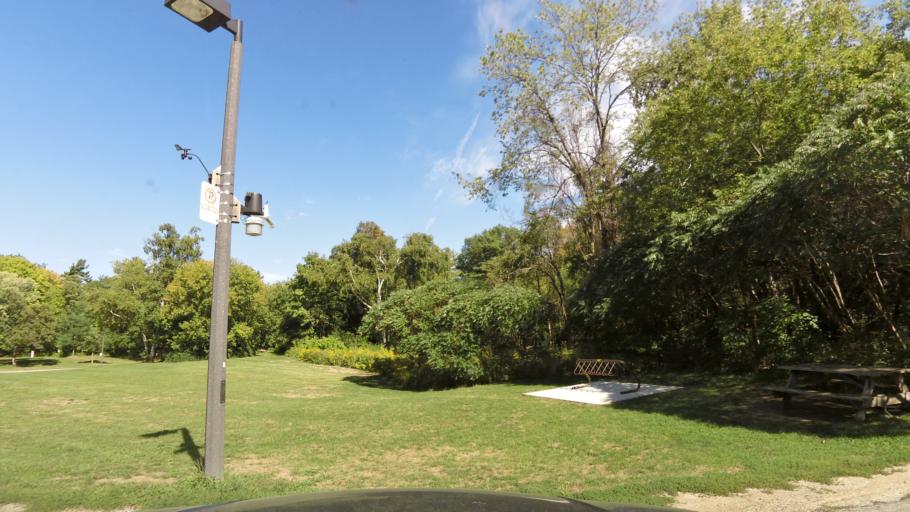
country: CA
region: Ontario
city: Mississauga
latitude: 43.5653
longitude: -79.6737
